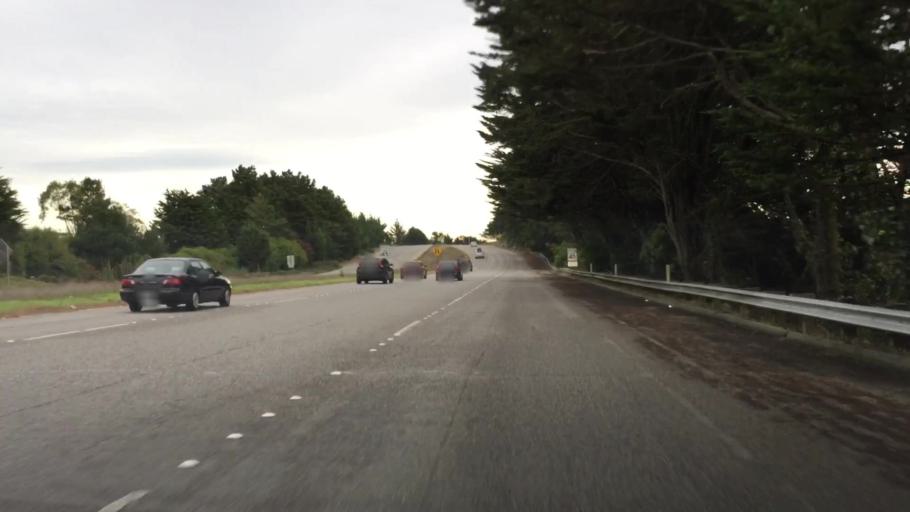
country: US
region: California
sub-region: San Mateo County
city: Broadmoor
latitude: 37.6650
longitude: -122.4804
